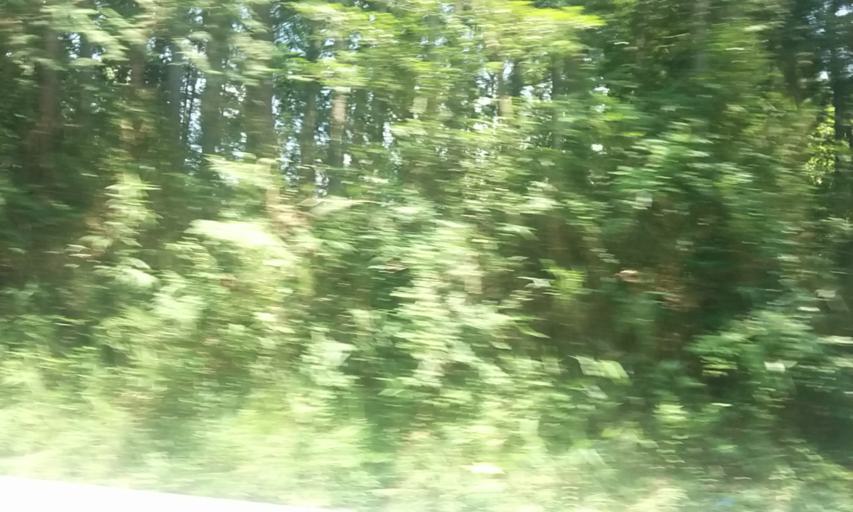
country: JP
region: Kyoto
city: Fukuchiyama
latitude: 35.2595
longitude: 135.1463
